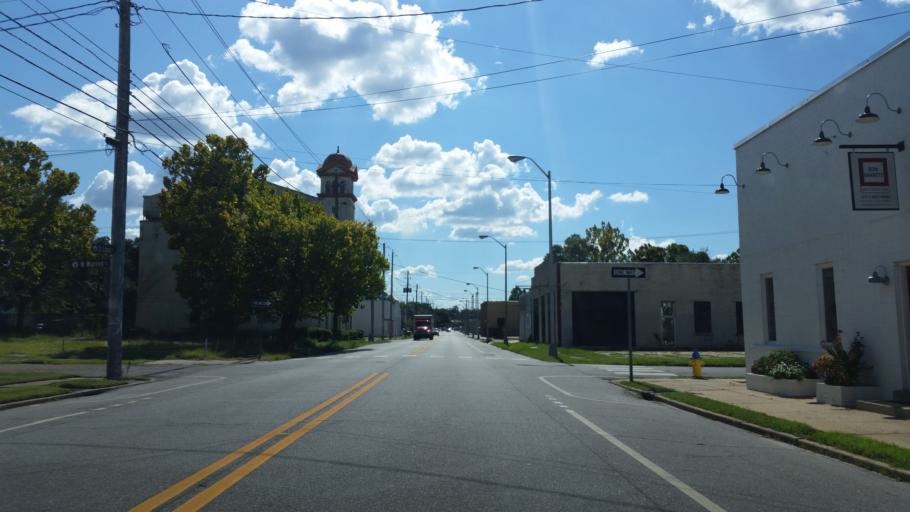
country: US
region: Alabama
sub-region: Mobile County
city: Mobile
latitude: 30.6918
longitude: -88.0504
